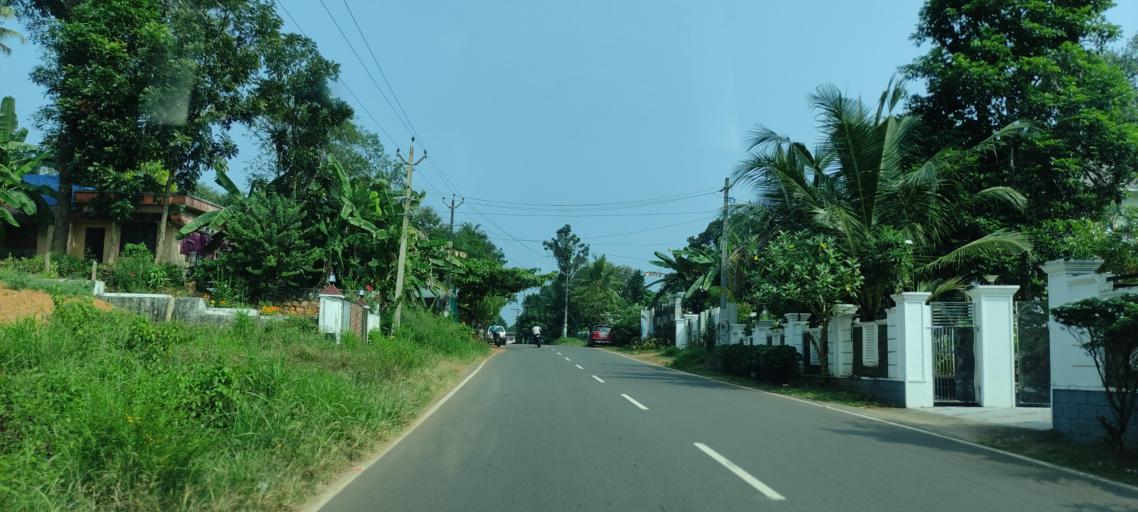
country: IN
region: Kerala
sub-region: Pattanamtitta
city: Adur
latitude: 9.2430
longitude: 76.6782
